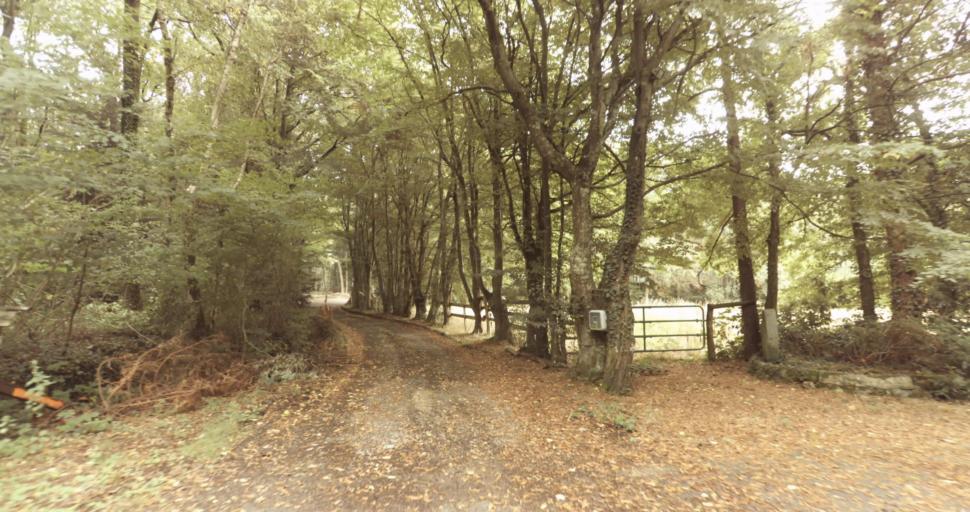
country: FR
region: Lower Normandy
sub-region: Departement de l'Orne
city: Aube-sur-Rile
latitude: 48.7518
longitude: 0.4923
